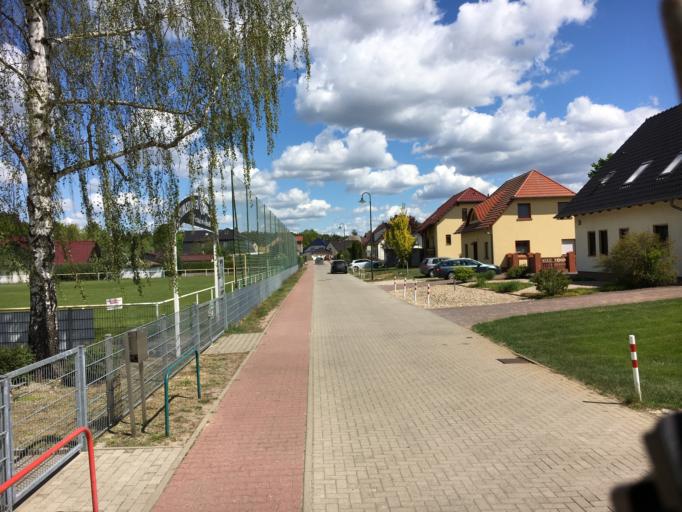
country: DE
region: Brandenburg
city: Luckenwalde
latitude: 52.1289
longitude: 13.1660
